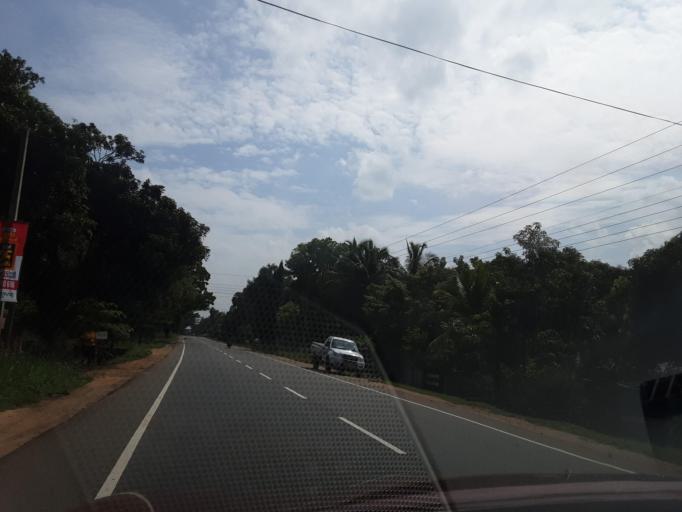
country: LK
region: Northern Province
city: Vavuniya
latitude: 8.5259
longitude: 80.4997
